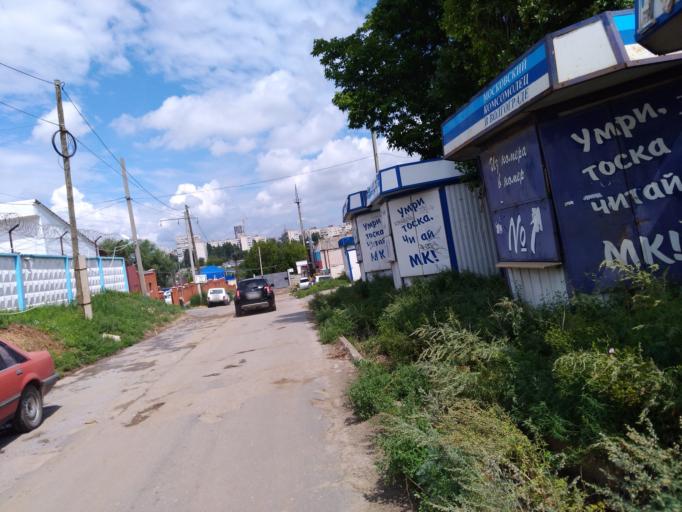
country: RU
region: Volgograd
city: Volgograd
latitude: 48.7121
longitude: 44.4620
